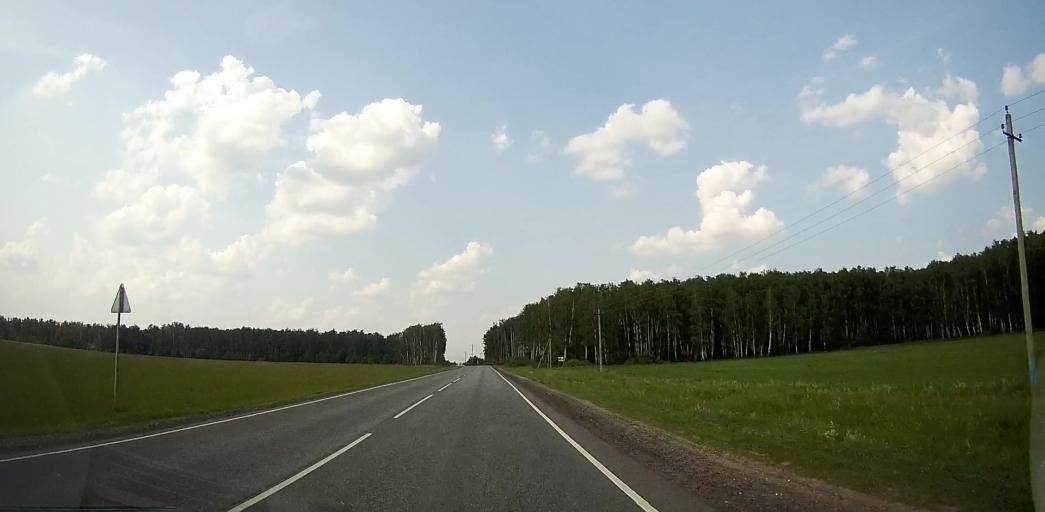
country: RU
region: Moskovskaya
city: Malino
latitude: 55.0508
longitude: 38.1455
